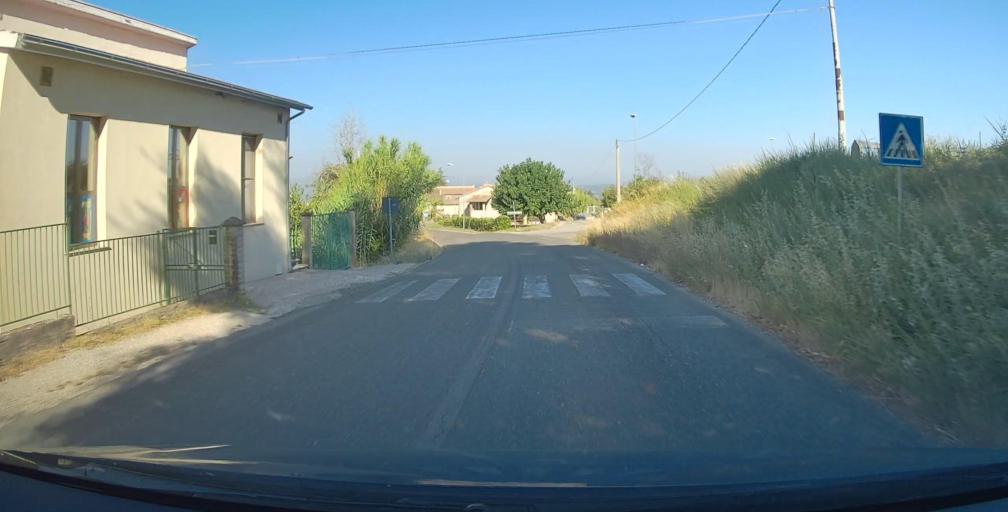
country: IT
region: Umbria
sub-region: Provincia di Terni
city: Calvi dell'Umbria
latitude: 42.4140
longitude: 12.5469
